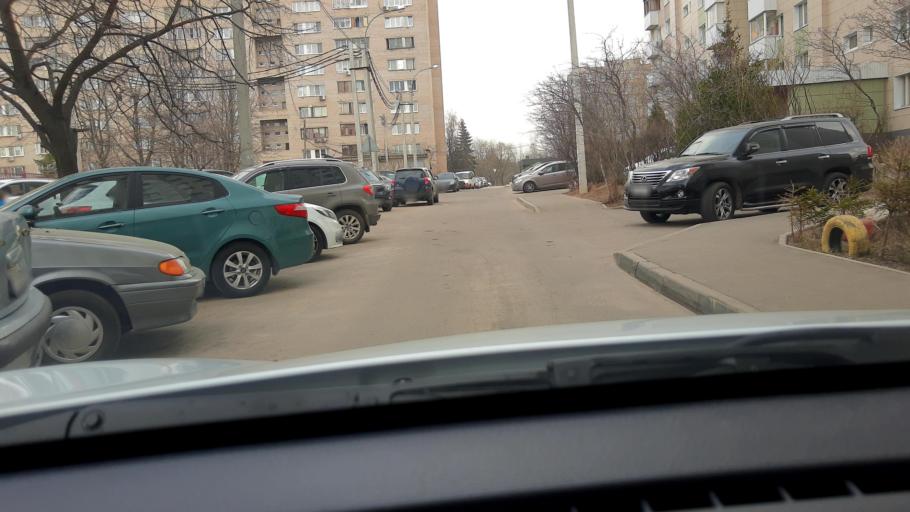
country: RU
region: Moskovskaya
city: Vostryakovo
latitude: 55.4166
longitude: 37.8335
